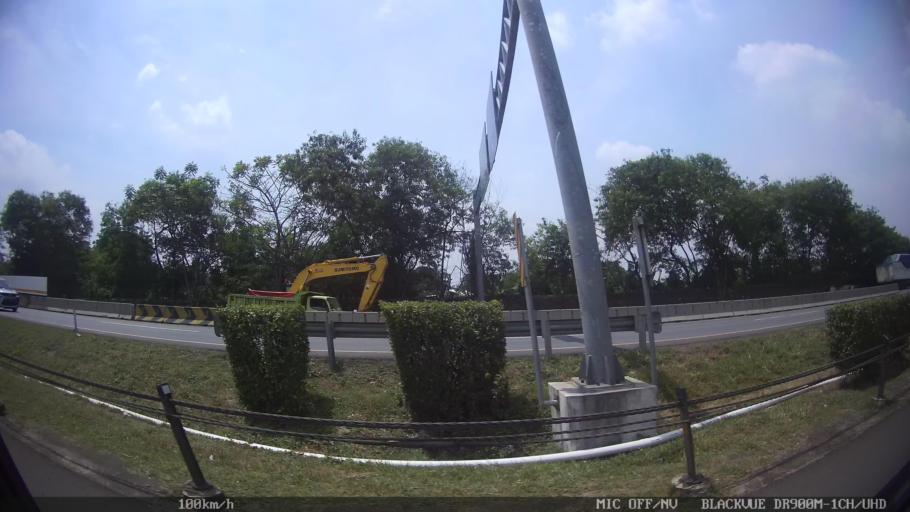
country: ID
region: Banten
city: Serang
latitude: -6.1385
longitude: 106.2375
